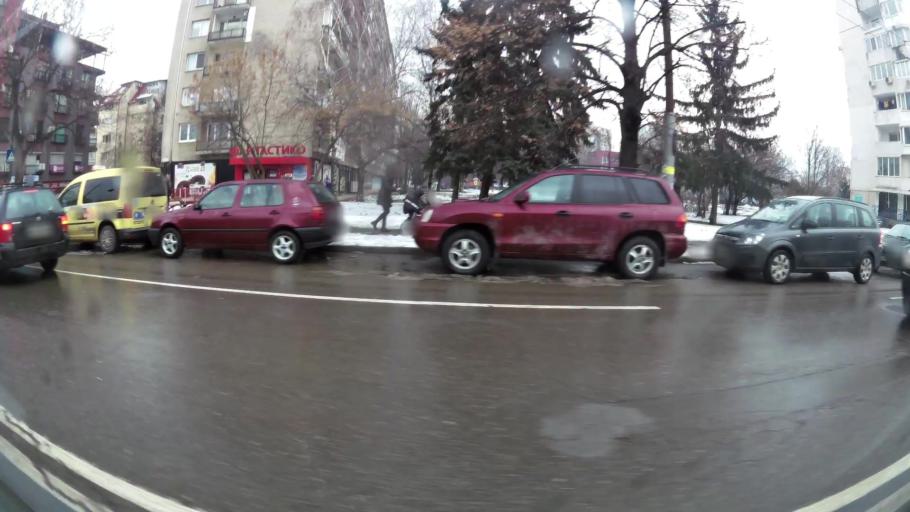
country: BG
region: Sofia-Capital
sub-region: Stolichna Obshtina
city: Sofia
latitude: 42.6722
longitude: 23.2844
